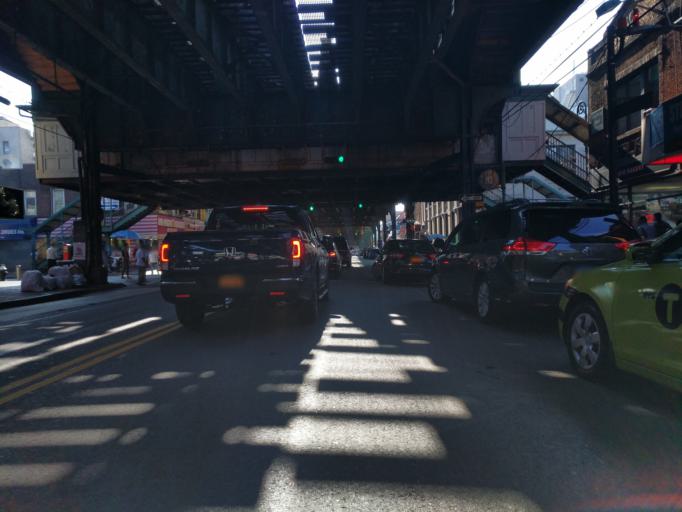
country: US
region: New York
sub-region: Queens County
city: Long Island City
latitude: 40.7478
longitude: -73.8831
